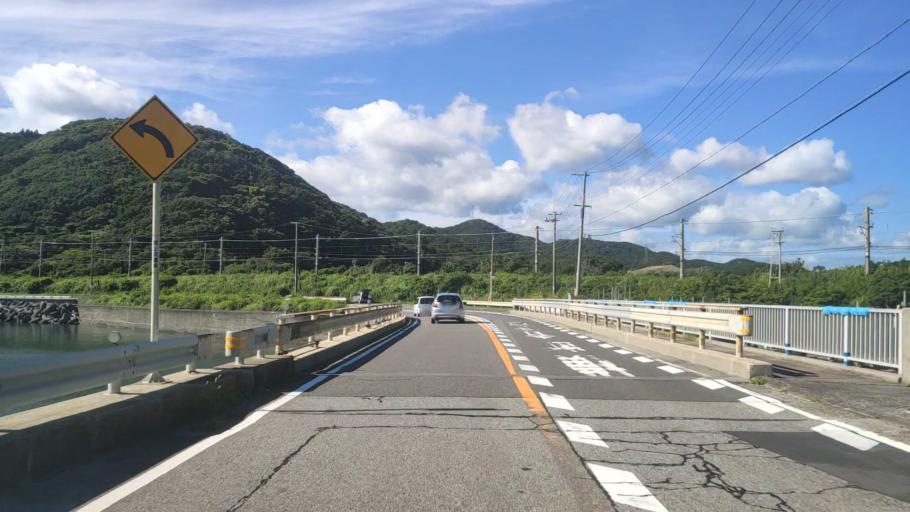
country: JP
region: Wakayama
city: Shingu
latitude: 33.4781
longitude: 135.7748
